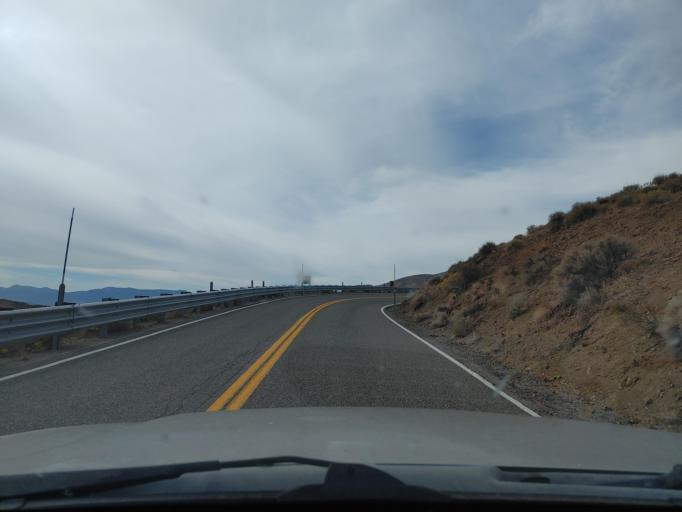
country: US
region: Nevada
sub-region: Storey County
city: Virginia City
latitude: 39.2725
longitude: -119.6276
